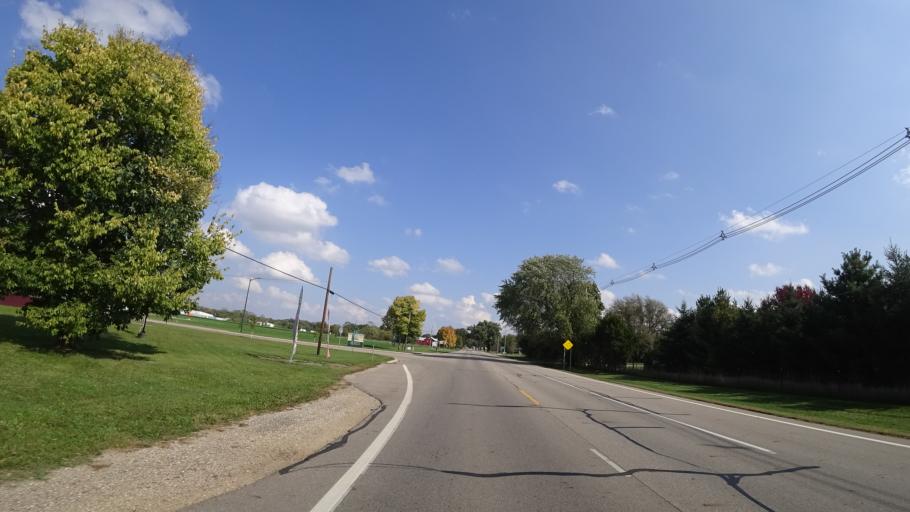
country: US
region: Michigan
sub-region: Saint Joseph County
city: Centreville
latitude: 42.0064
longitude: -85.4674
